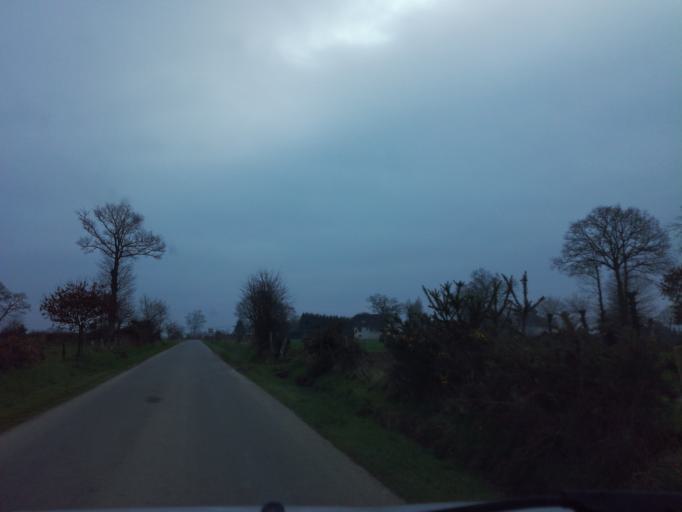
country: FR
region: Brittany
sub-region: Departement d'Ille-et-Vilaine
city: Gosne
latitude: 48.2607
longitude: -1.4537
